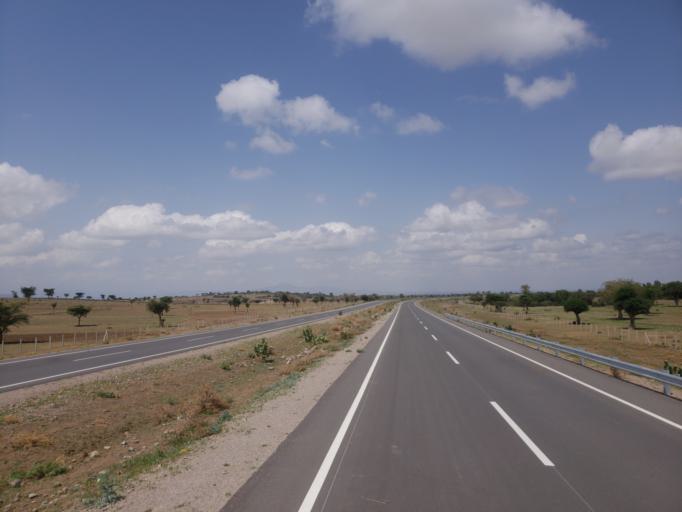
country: ET
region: Oromiya
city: Mojo
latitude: 8.5192
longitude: 39.0897
